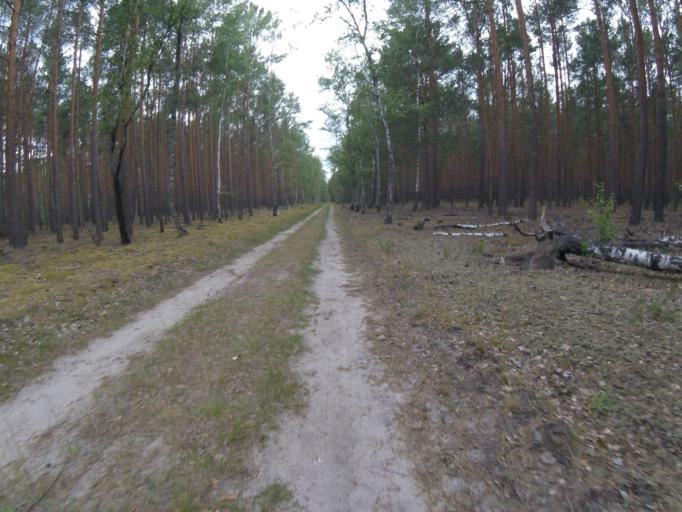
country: DE
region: Brandenburg
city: Halbe
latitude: 52.1762
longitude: 13.7484
